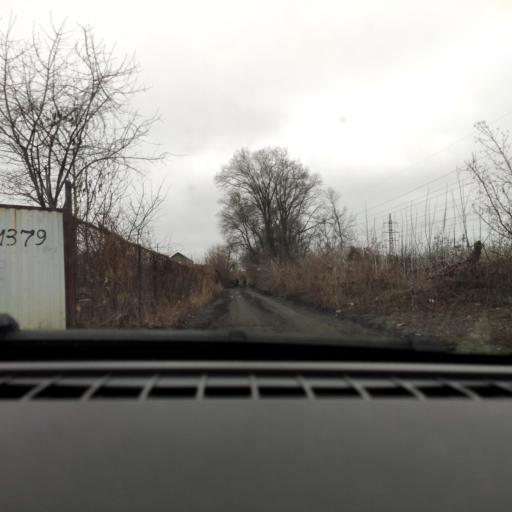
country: RU
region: Voronezj
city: Maslovka
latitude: 51.6082
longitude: 39.2720
